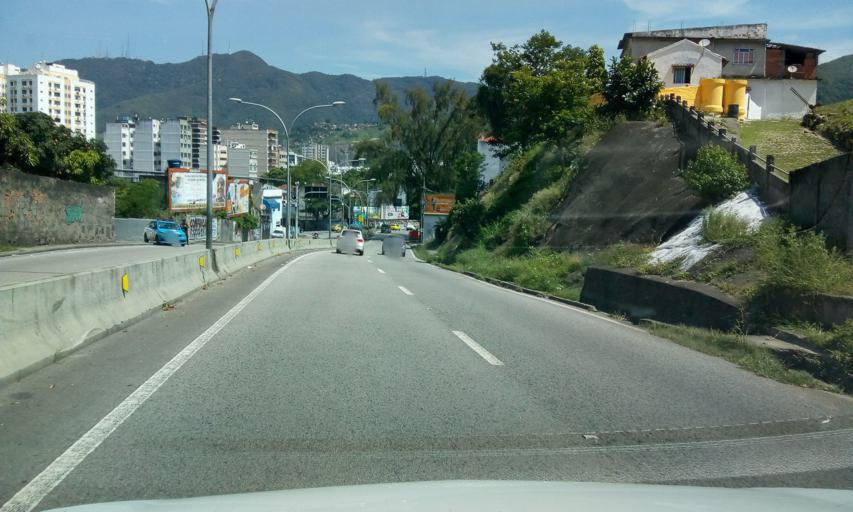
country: BR
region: Rio de Janeiro
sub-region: Rio De Janeiro
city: Rio de Janeiro
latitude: -22.9157
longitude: -43.2635
